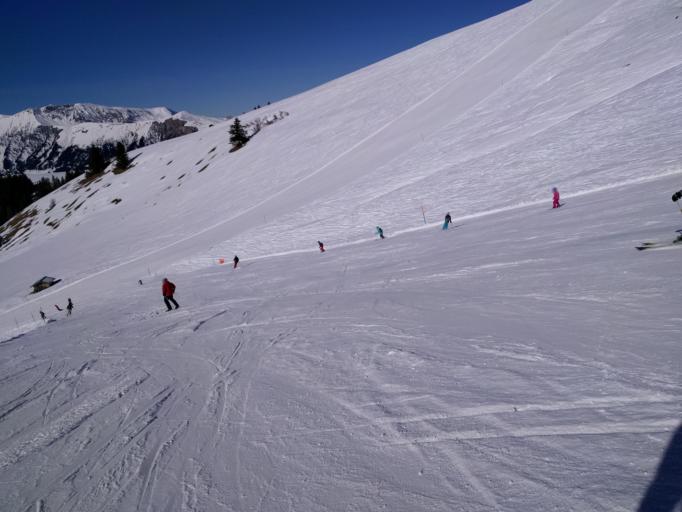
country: CH
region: Bern
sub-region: Obersimmental-Saanen District
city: Lenk
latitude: 46.4508
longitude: 7.4907
